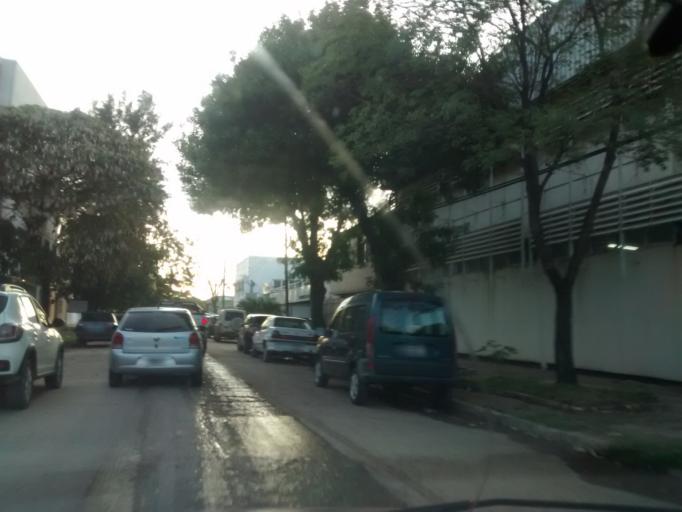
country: AR
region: Chaco
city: Resistencia
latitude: -27.4400
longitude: -58.9973
